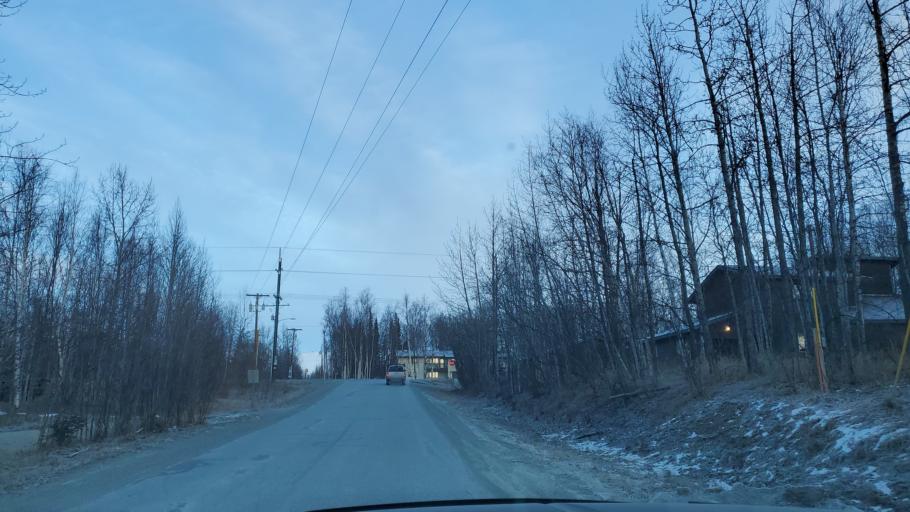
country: US
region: Alaska
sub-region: Matanuska-Susitna Borough
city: Lakes
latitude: 61.6130
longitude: -149.3064
